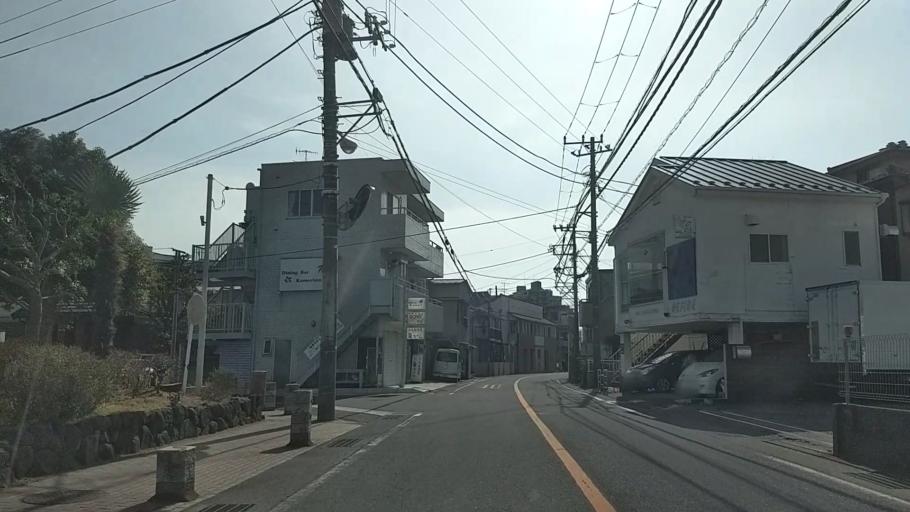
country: JP
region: Kanagawa
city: Chigasaki
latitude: 35.3357
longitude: 139.3828
